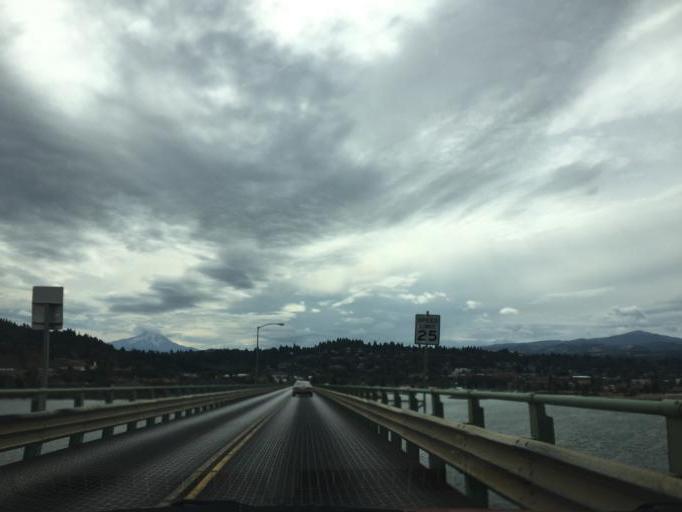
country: US
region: Washington
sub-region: Klickitat County
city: White Salmon
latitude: 45.7178
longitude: -121.4954
